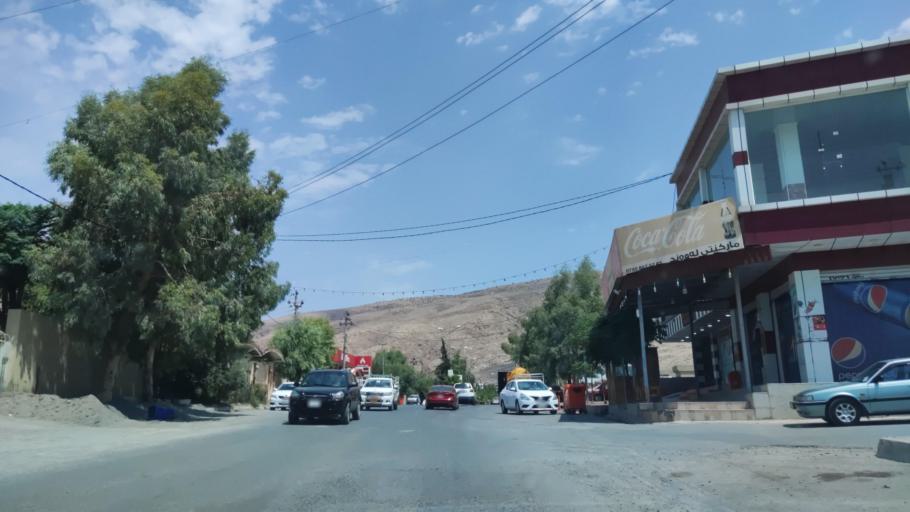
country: IQ
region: Arbil
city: Shaqlawah
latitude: 36.5453
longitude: 44.3486
